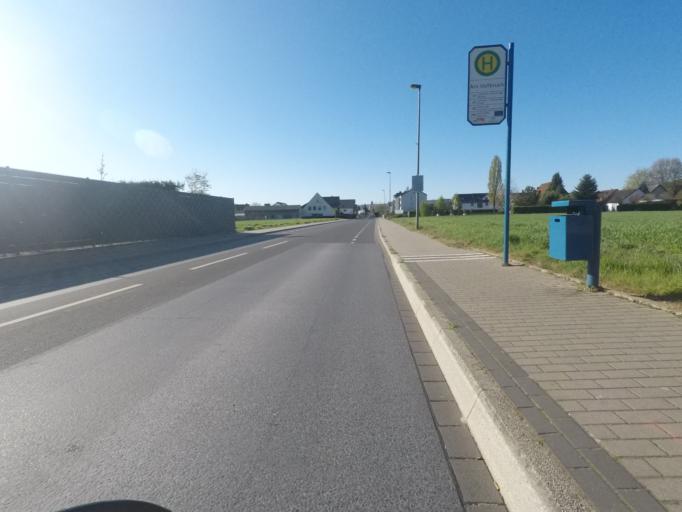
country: DE
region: North Rhine-Westphalia
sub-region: Regierungsbezirk Detmold
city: Bielefeld
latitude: 52.0167
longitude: 8.5978
